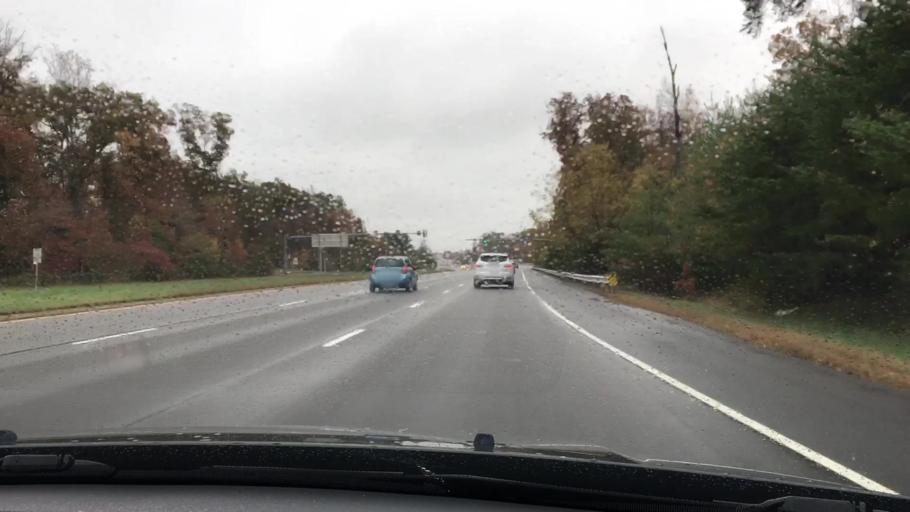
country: US
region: Virginia
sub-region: Fairfax County
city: Lorton
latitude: 38.7075
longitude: -77.2608
